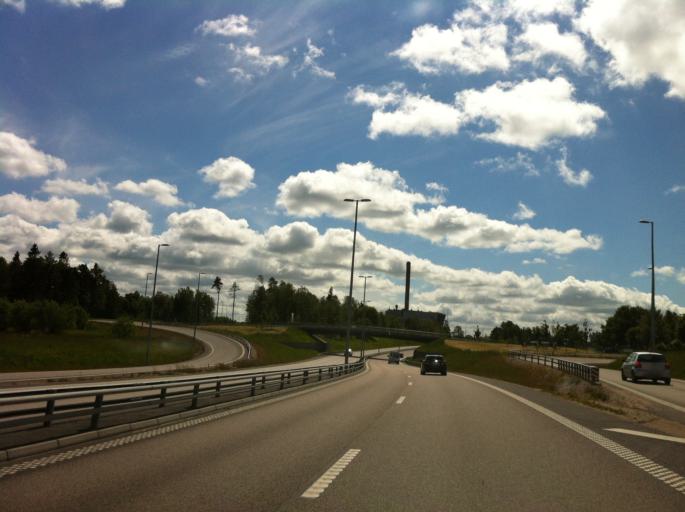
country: SE
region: Vaestra Goetaland
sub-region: Trollhattan
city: Trollhattan
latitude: 58.2585
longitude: 12.2836
